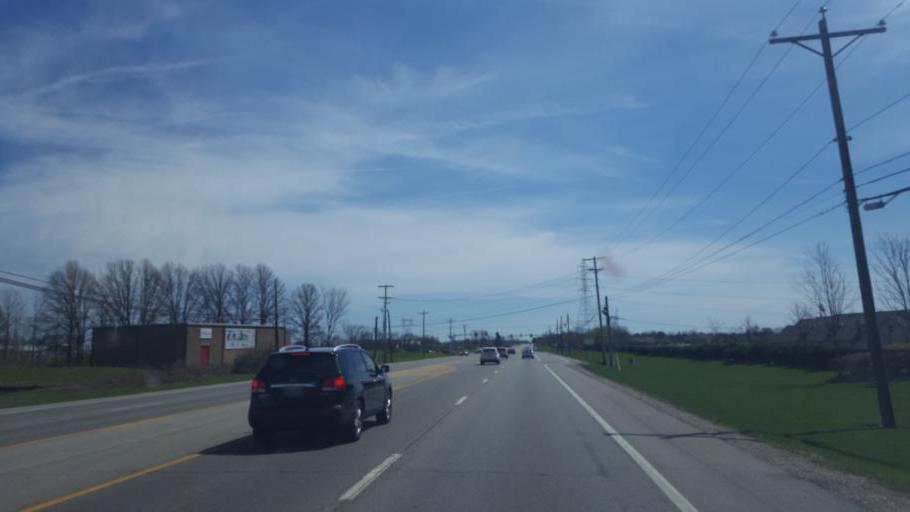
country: US
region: Ohio
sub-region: Delaware County
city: Lewis Center
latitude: 40.1903
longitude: -83.0262
